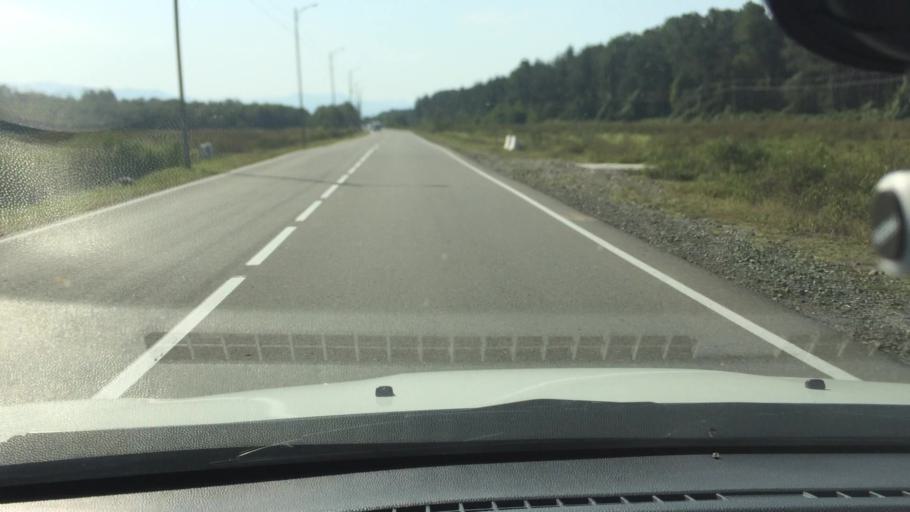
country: GE
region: Guria
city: Urek'i
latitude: 41.9500
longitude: 41.7701
